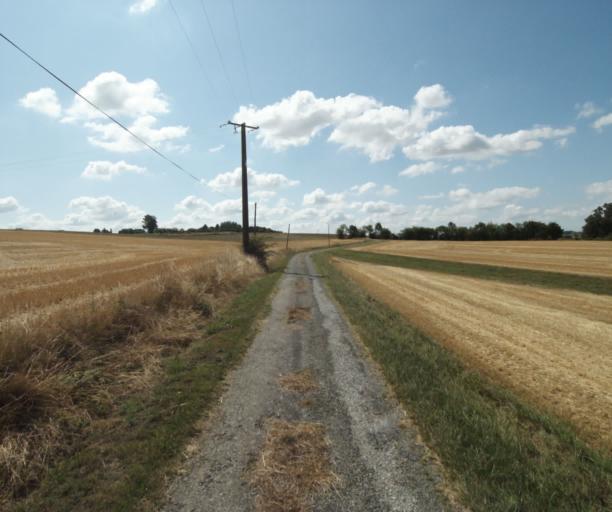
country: FR
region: Midi-Pyrenees
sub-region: Departement de la Haute-Garonne
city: Caraman
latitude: 43.4537
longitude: 1.7835
